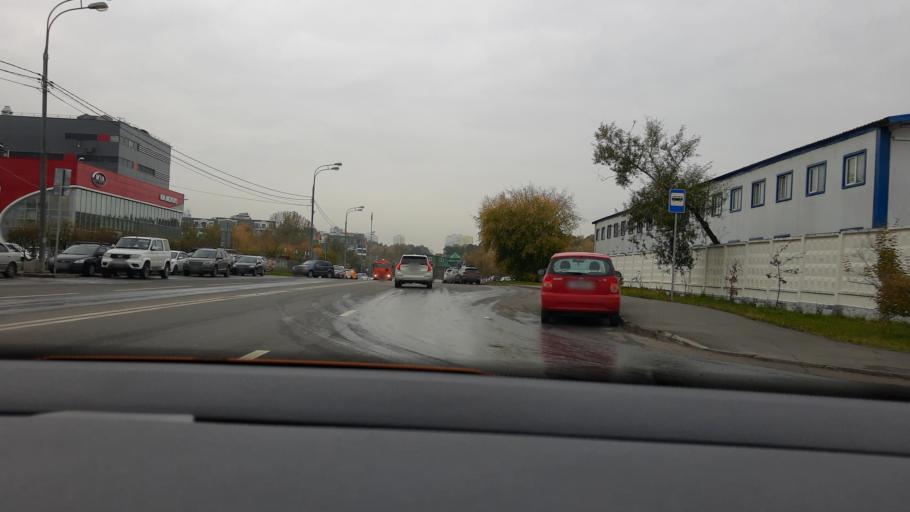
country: RU
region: Moscow
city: Strogino
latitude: 55.7722
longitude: 37.4042
